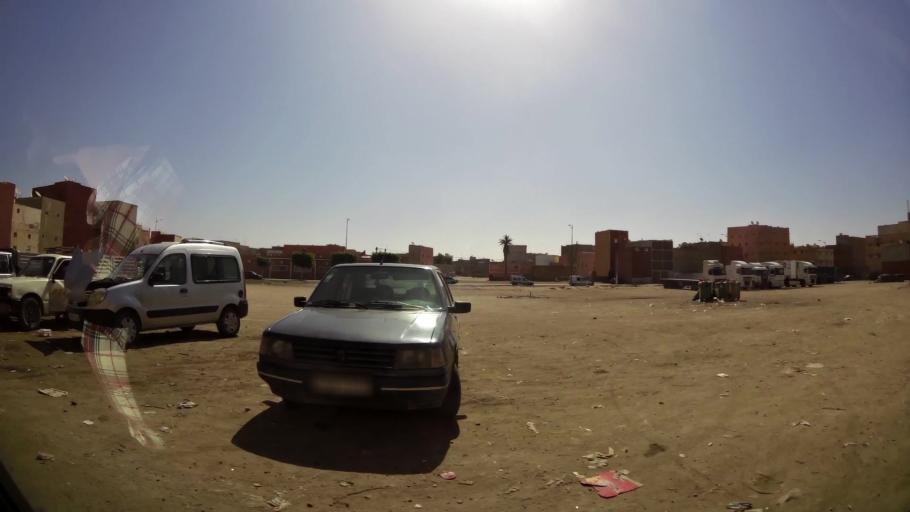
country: MA
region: Souss-Massa-Draa
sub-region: Inezgane-Ait Mellou
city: Inezgane
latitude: 30.3478
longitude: -9.5080
